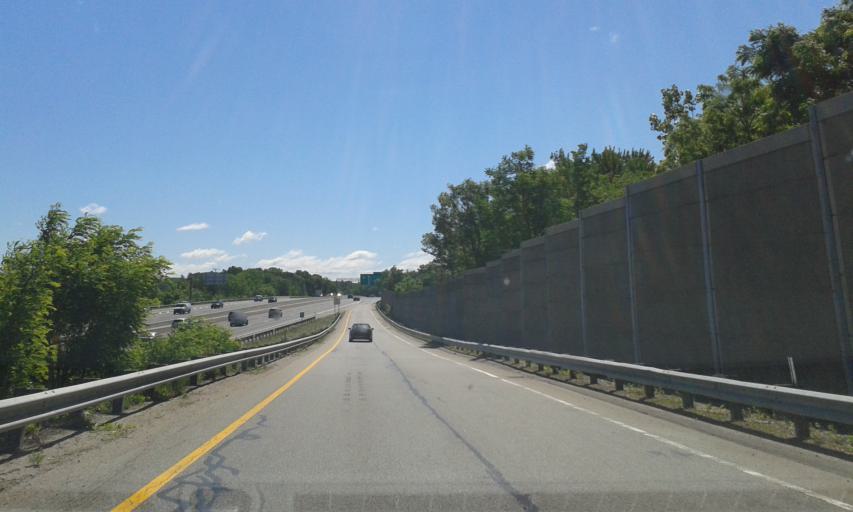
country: US
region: Massachusetts
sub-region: Middlesex County
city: Chelmsford
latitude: 42.6216
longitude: -71.3646
